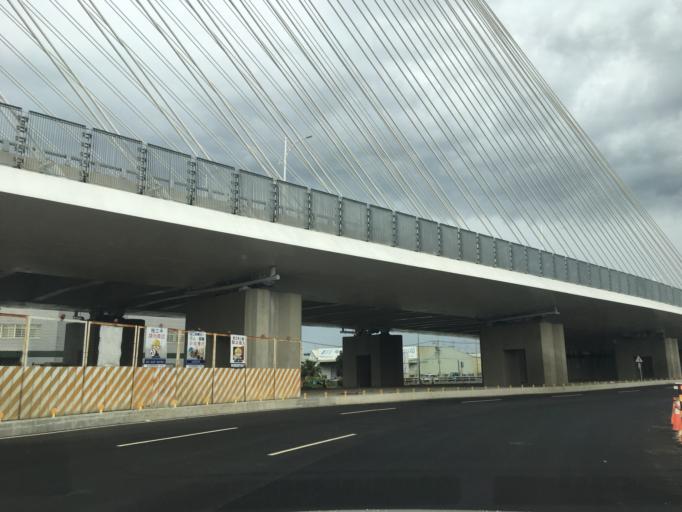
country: TW
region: Taiwan
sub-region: Taichung City
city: Taichung
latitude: 24.1987
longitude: 120.6519
